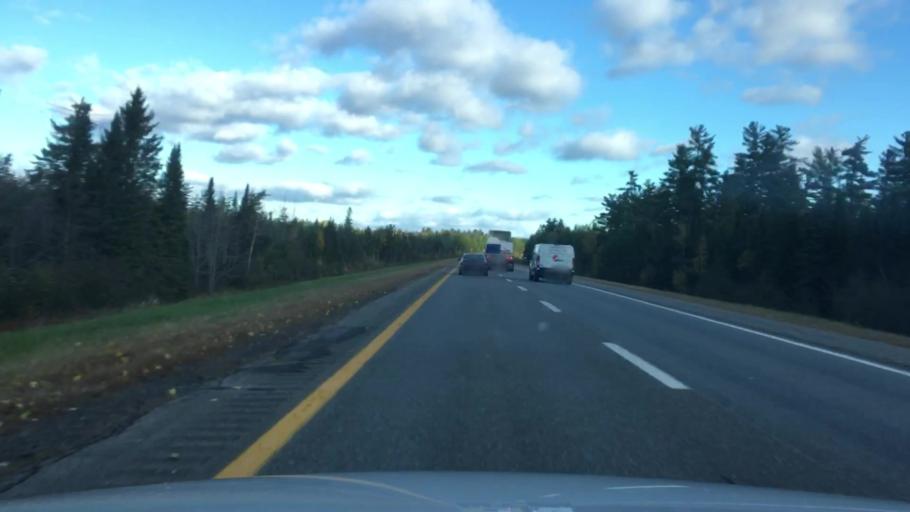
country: US
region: Maine
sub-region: Penobscot County
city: Greenbush
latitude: 45.1453
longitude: -68.7021
